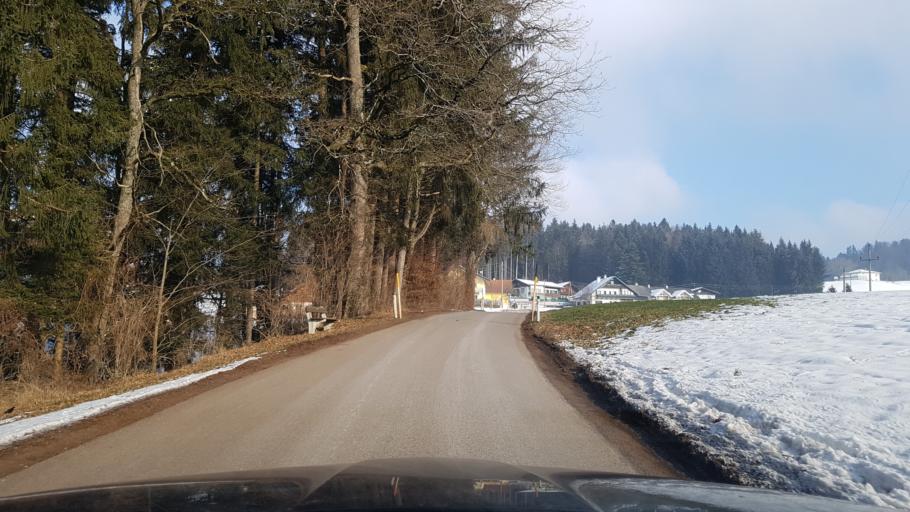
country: AT
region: Salzburg
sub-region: Politischer Bezirk Salzburg-Umgebung
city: Thalgau
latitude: 47.8579
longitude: 13.2322
